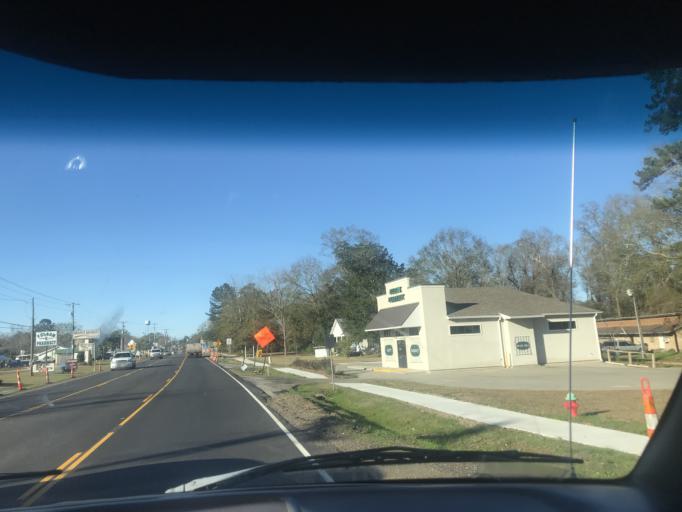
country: US
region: Louisiana
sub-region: Saint Tammany Parish
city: Covington
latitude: 30.6261
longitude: -90.1864
